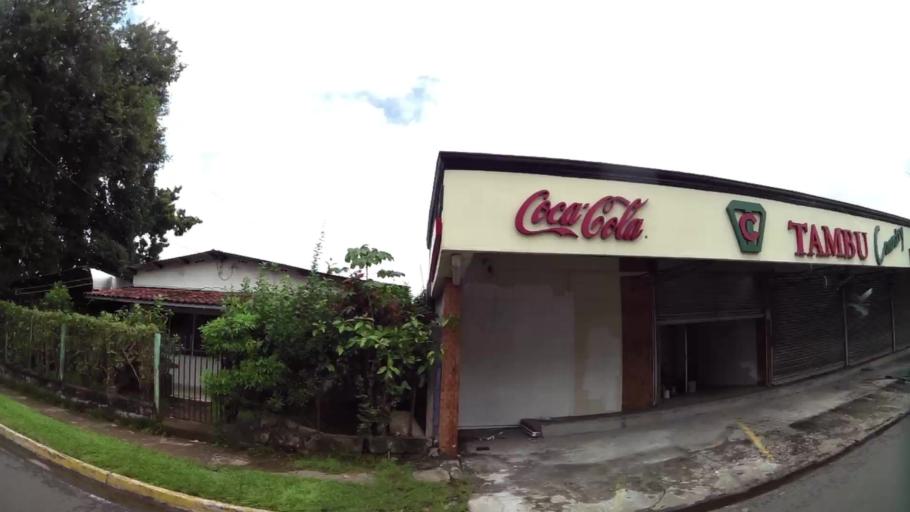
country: PA
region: Chiriqui
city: David
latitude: 8.4230
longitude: -82.4294
